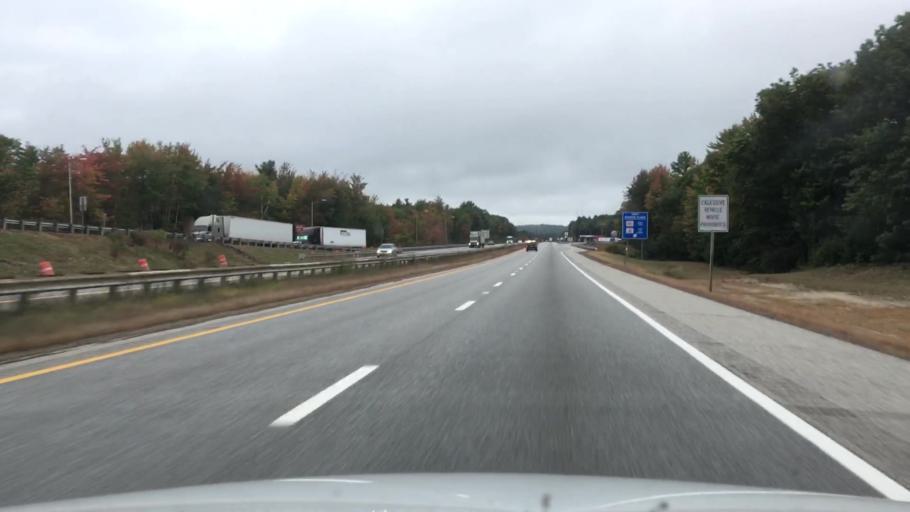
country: US
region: Maine
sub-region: Cumberland County
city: Cumberland Center
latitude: 43.8185
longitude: -70.3191
